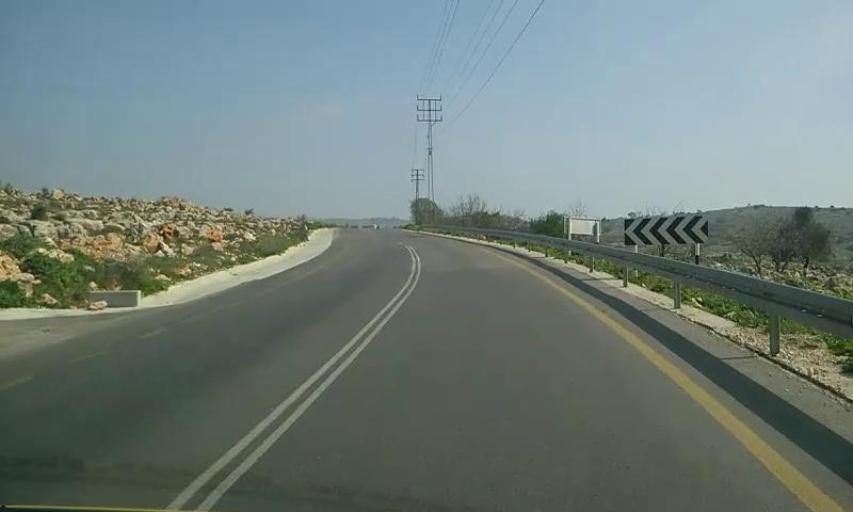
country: PS
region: West Bank
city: Silwad
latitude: 31.9655
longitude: 35.2661
